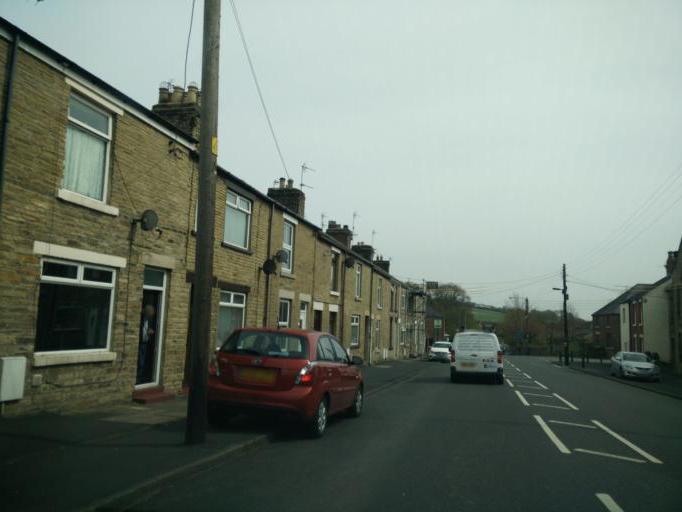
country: GB
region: England
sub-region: County Durham
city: Crook
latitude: 54.6948
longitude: -1.7487
